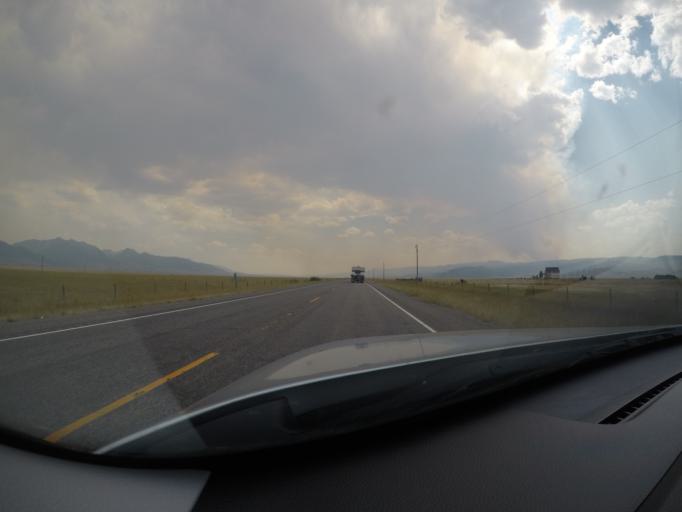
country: US
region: Montana
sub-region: Madison County
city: Virginia City
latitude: 45.1605
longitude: -111.6786
